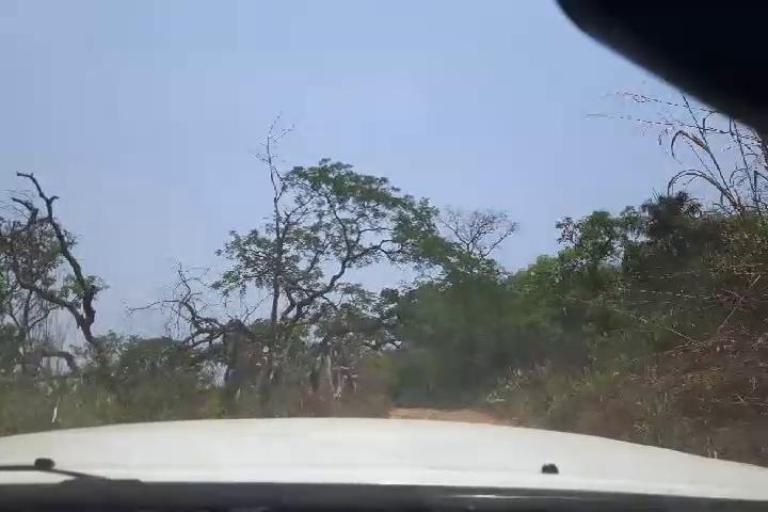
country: SL
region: Northern Province
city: Alikalia
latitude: 9.0816
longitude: -11.4680
